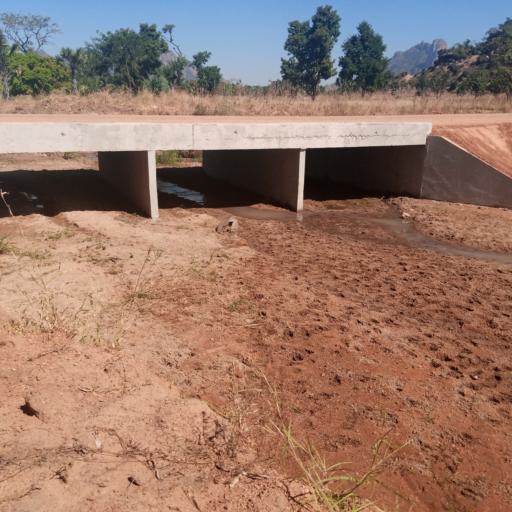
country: NG
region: Adamawa
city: Little Gombi
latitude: 10.1692
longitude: 12.8898
